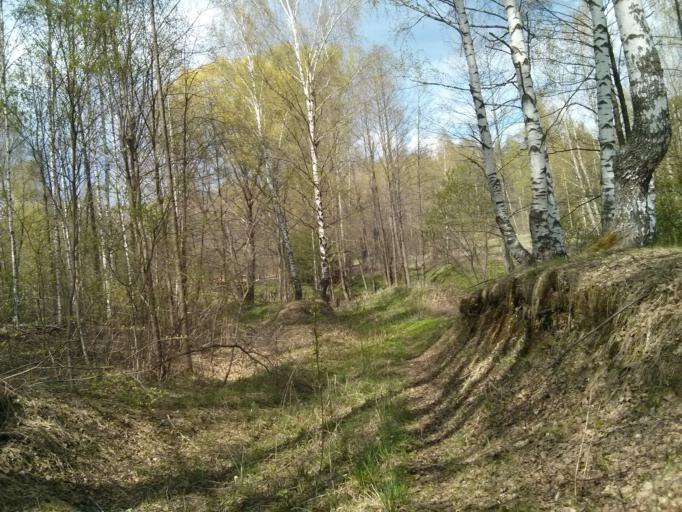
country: RU
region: Nizjnij Novgorod
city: Shimorskoye
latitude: 55.3069
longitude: 41.8537
